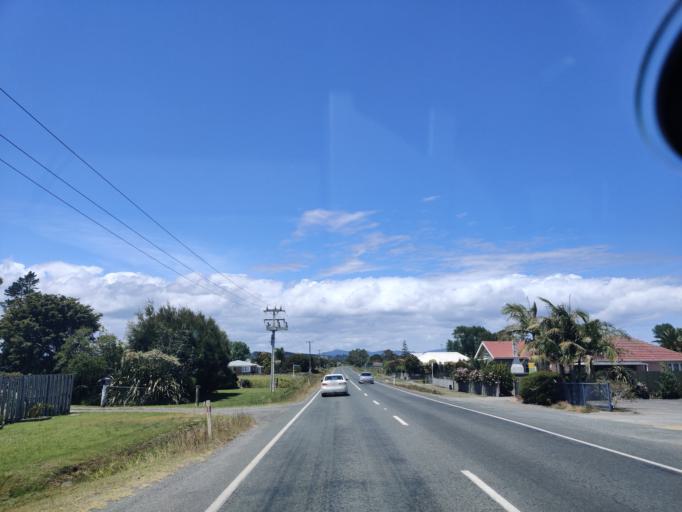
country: NZ
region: Northland
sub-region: Far North District
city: Kaitaia
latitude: -35.0393
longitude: 173.2552
